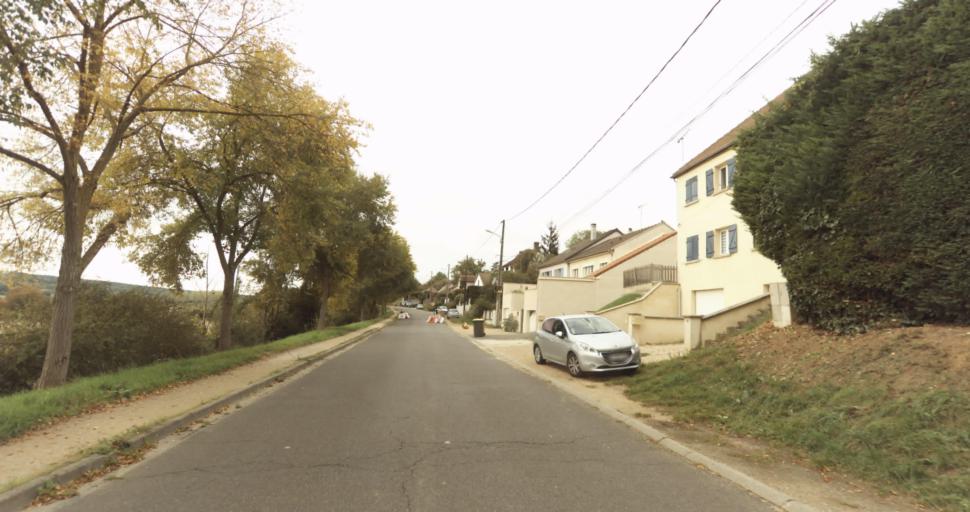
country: FR
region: Centre
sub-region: Departement d'Eure-et-Loir
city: Dreux
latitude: 48.7262
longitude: 1.3504
